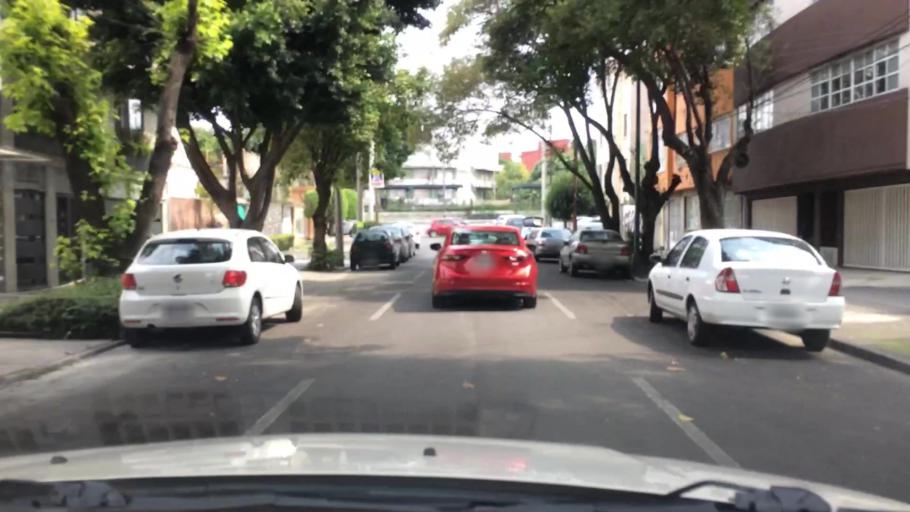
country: MX
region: Mexico City
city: Benito Juarez
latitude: 19.4022
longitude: -99.1655
